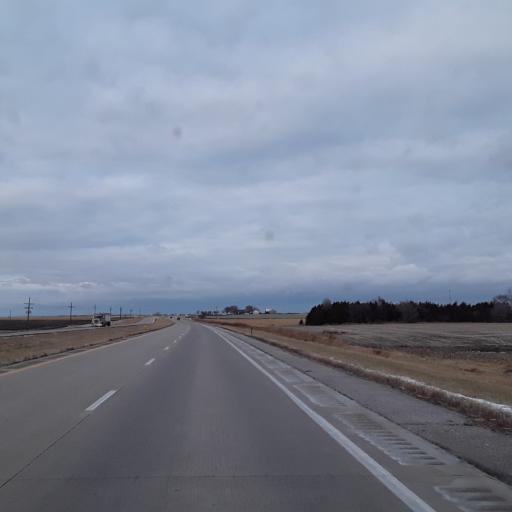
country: US
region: Nebraska
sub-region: Thayer County
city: Hebron
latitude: 40.3446
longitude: -97.5767
